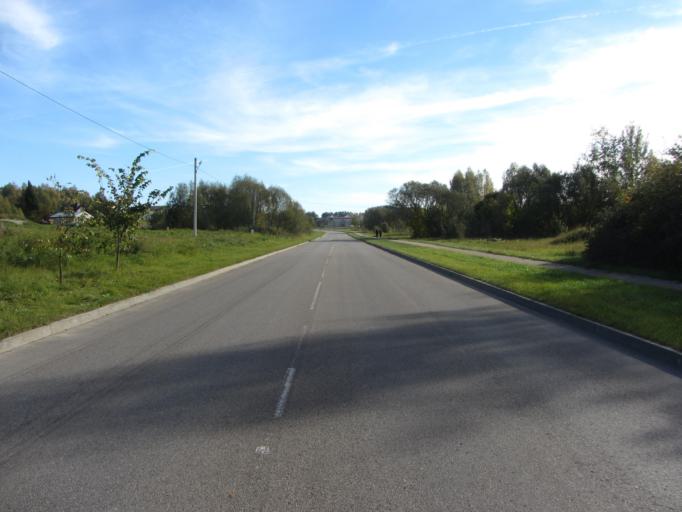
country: LT
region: Vilnius County
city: Elektrenai
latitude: 54.7856
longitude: 24.6873
